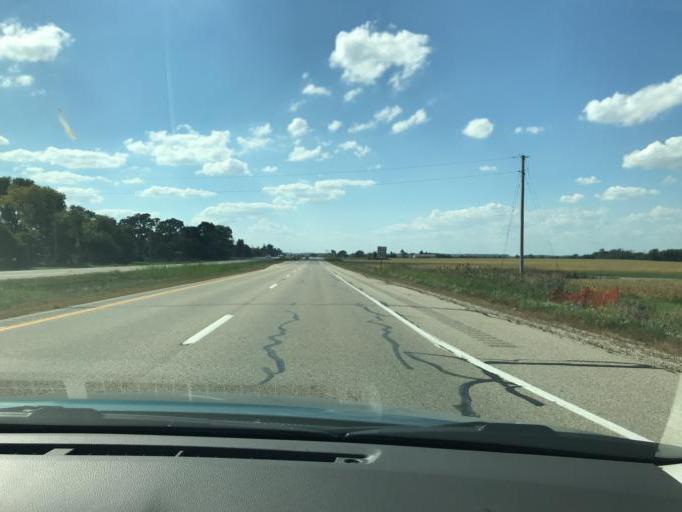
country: US
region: Wisconsin
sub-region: Walworth County
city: Pell Lake
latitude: 42.5968
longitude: -88.3650
